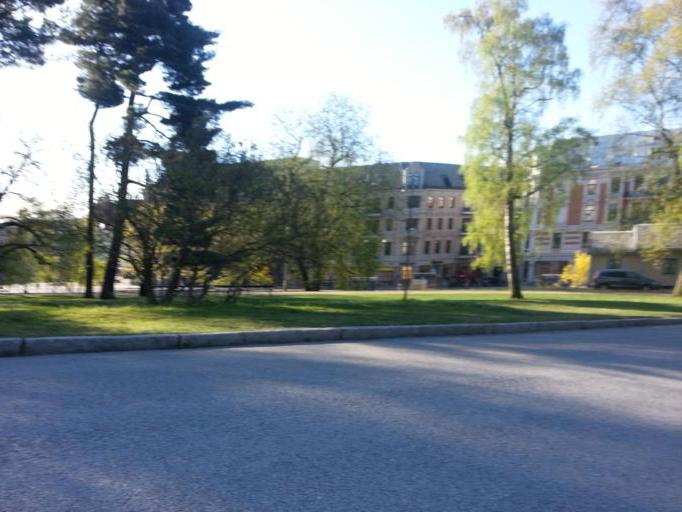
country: NO
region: Oslo
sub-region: Oslo
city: Oslo
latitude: 59.9160
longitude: 10.7274
